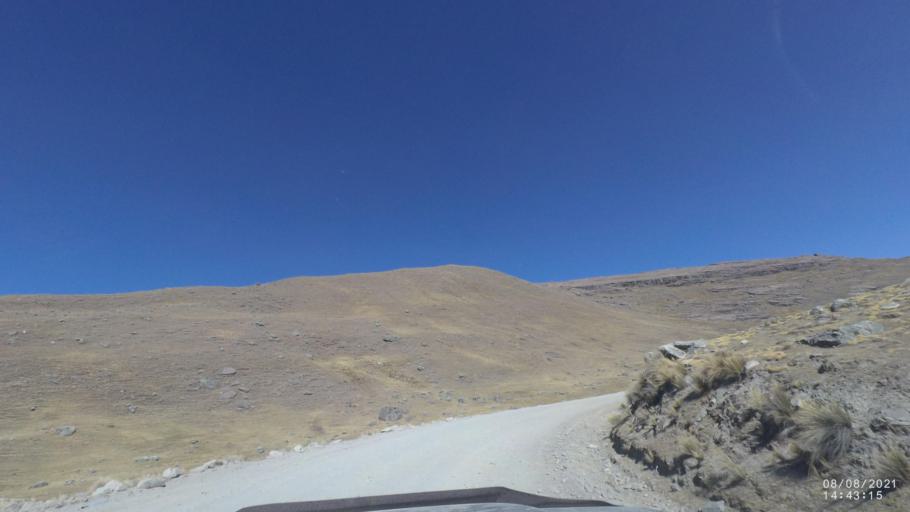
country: BO
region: Cochabamba
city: Sipe Sipe
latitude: -17.2241
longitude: -66.3826
